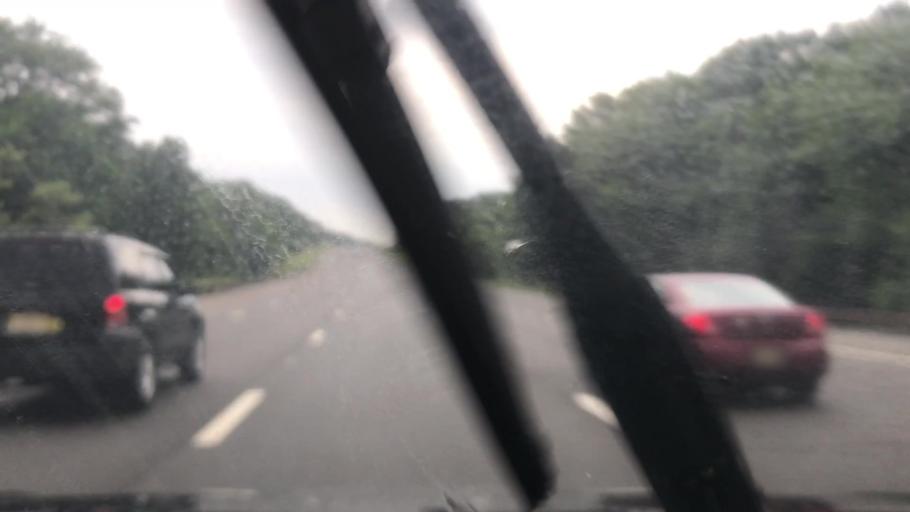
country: US
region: New Jersey
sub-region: Monmouth County
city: Wanamassa
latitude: 40.2456
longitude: -74.0846
